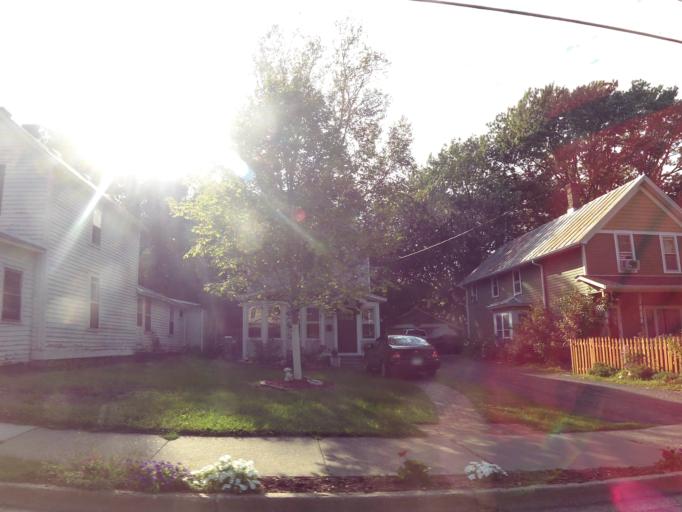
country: US
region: Minnesota
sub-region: Washington County
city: Stillwater
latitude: 45.0493
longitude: -92.8076
